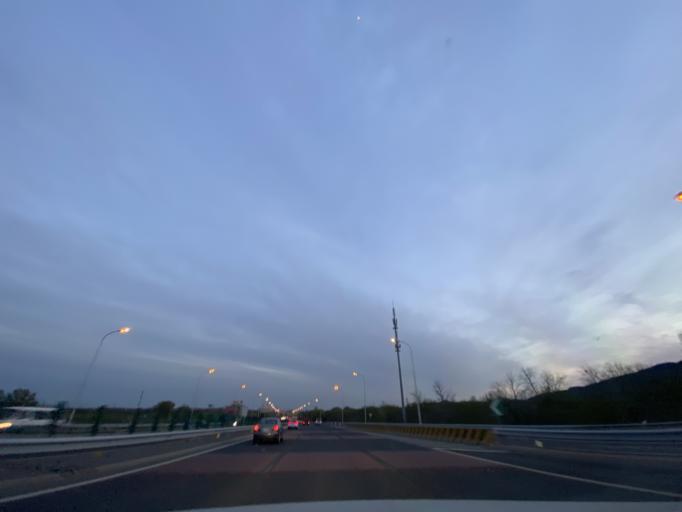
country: CN
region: Beijing
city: Xiangshan
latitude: 39.9884
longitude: 116.2150
